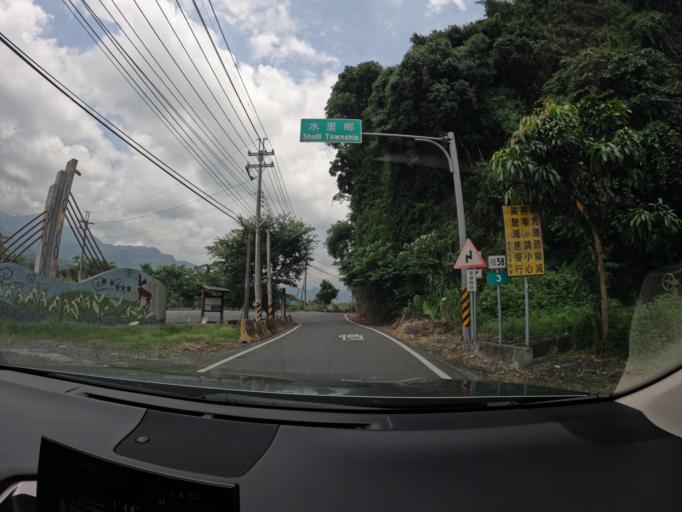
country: TW
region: Taiwan
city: Lugu
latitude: 23.8118
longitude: 120.8128
